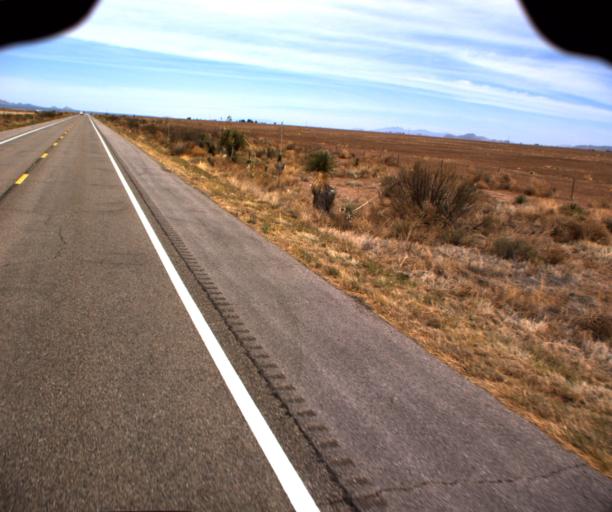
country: US
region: Arizona
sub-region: Cochise County
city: Pirtleville
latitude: 31.5459
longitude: -109.6597
